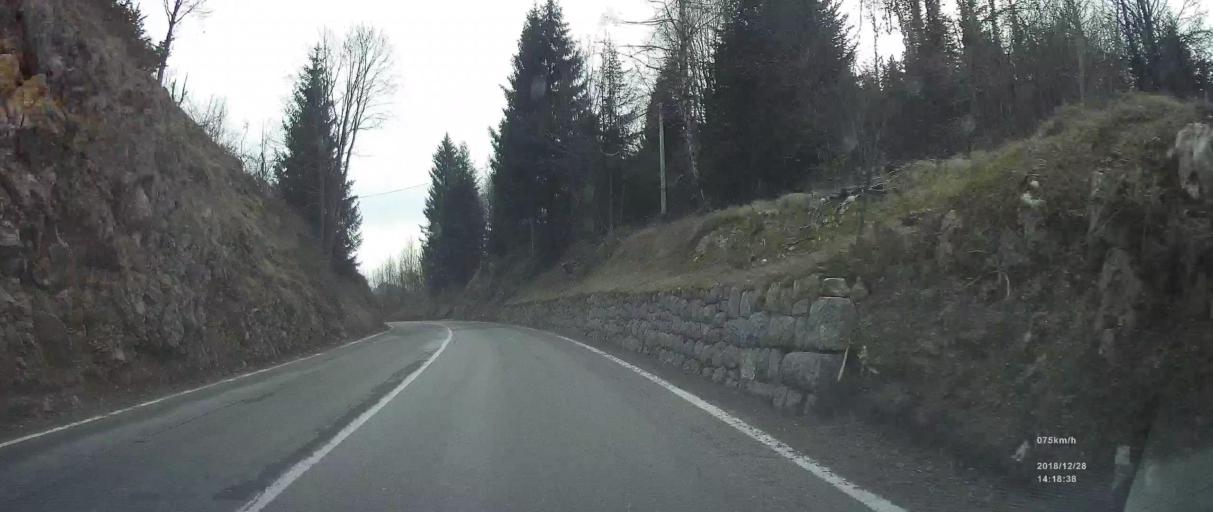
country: HR
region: Primorsko-Goranska
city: Vrbovsko
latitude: 45.4107
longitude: 15.0603
